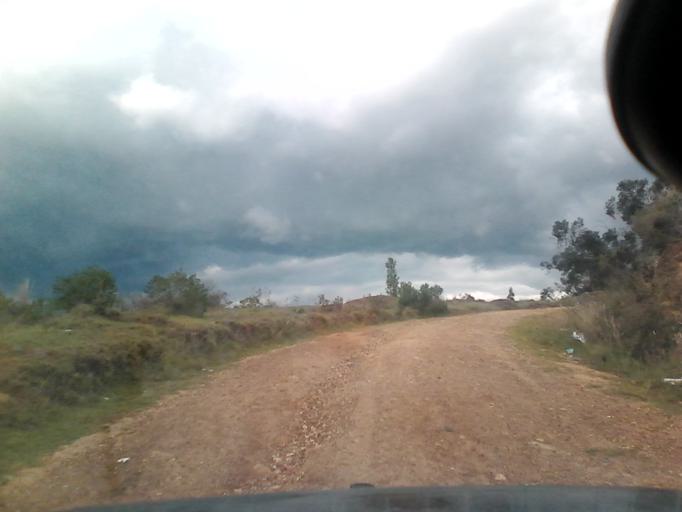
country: CO
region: Boyaca
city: Duitama
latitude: 5.8314
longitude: -73.0375
